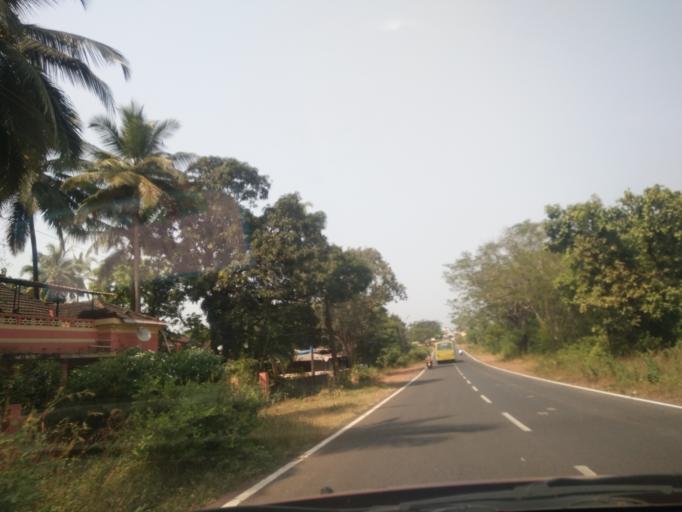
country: IN
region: Goa
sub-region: North Goa
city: Aldona
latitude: 15.6236
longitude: 73.8816
